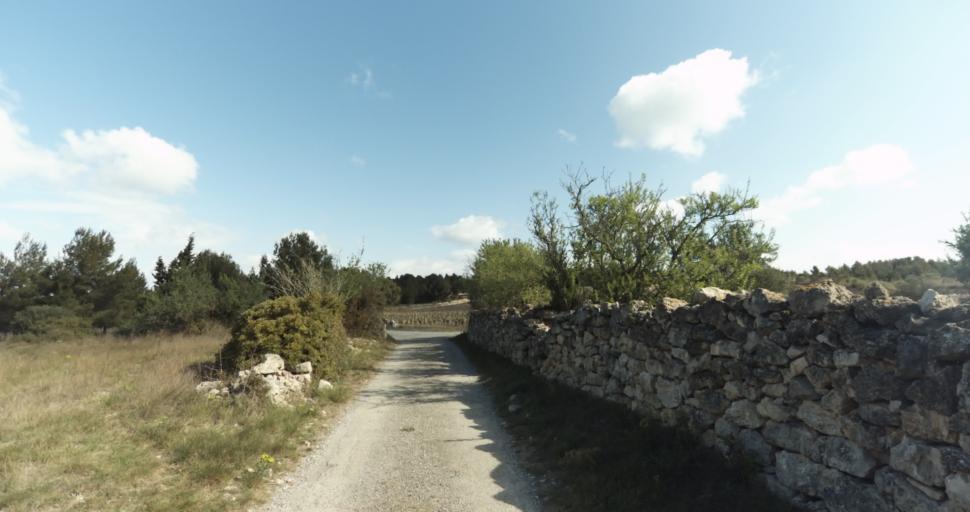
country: FR
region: Languedoc-Roussillon
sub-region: Departement de l'Aude
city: Leucate
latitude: 42.9283
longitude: 3.0308
